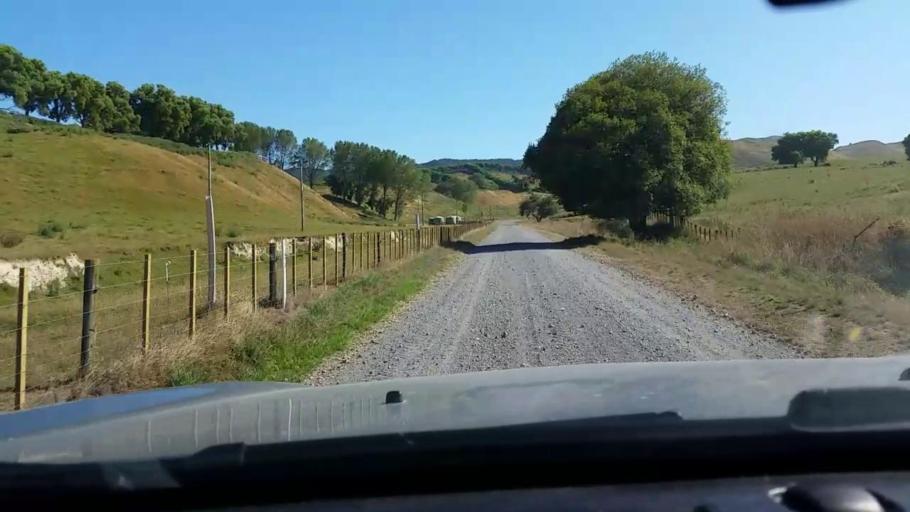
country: NZ
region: Bay of Plenty
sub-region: Rotorua District
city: Rotorua
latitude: -38.3157
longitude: 176.3018
